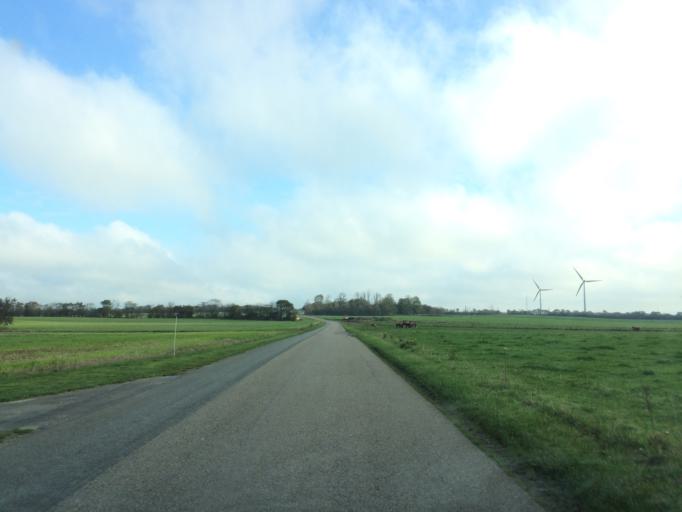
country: DK
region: Central Jutland
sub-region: Holstebro Kommune
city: Holstebro
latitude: 56.3514
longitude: 8.5311
